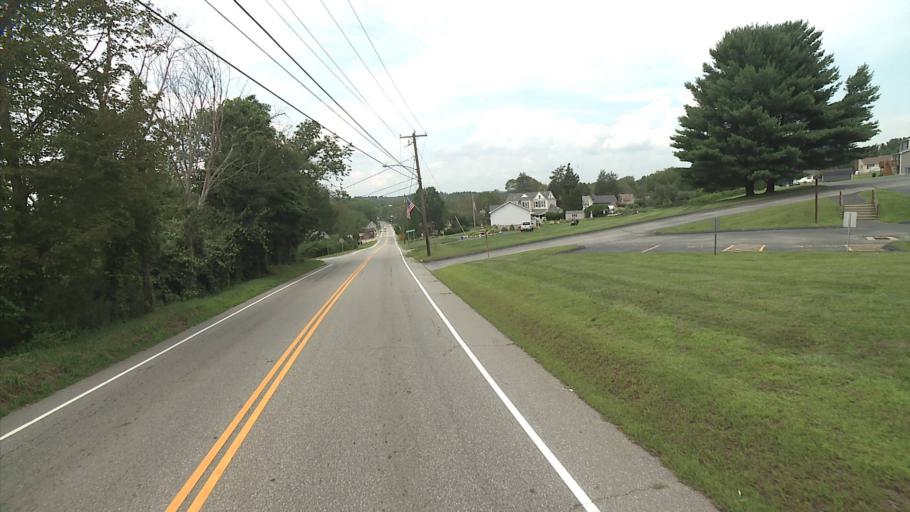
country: US
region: Connecticut
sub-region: Windham County
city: Wauregan
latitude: 41.7438
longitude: -71.9092
